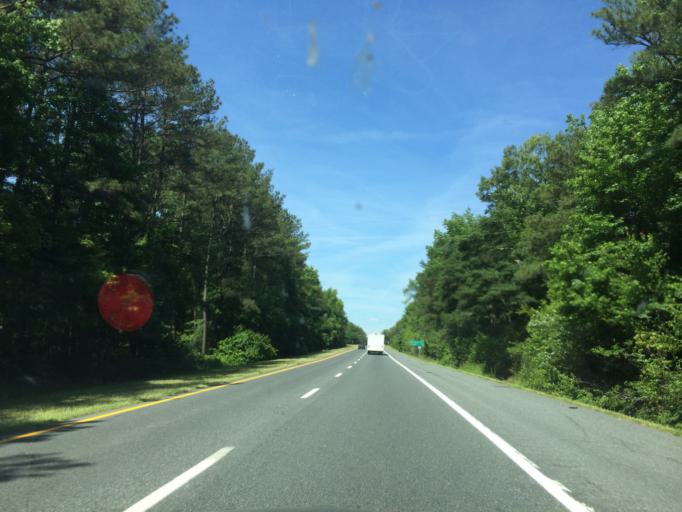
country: US
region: Maryland
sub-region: Wicomico County
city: Pittsville
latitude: 38.3854
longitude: -75.4261
